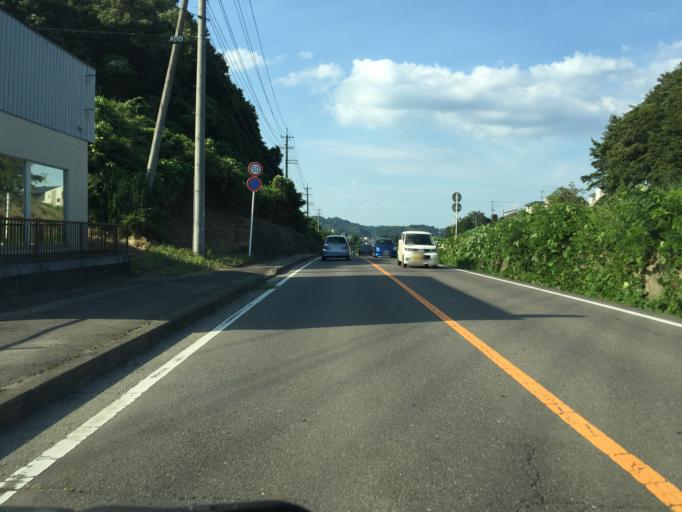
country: JP
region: Fukushima
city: Nihommatsu
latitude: 37.5729
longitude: 140.4160
